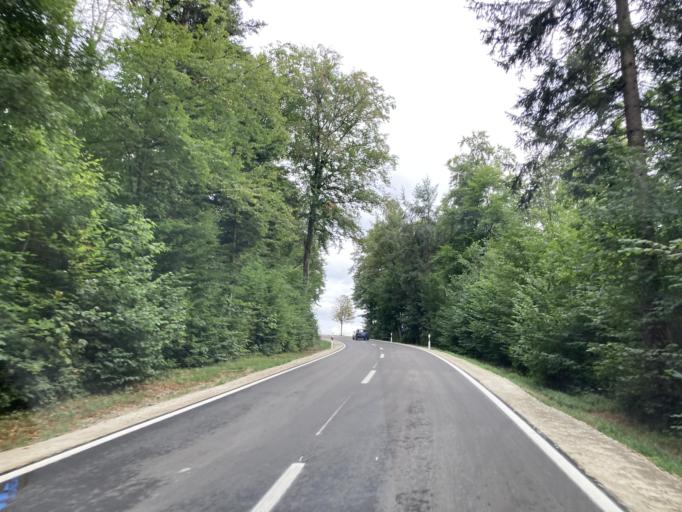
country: DE
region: Bavaria
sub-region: Swabia
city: Forheim
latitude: 48.7984
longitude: 10.4113
